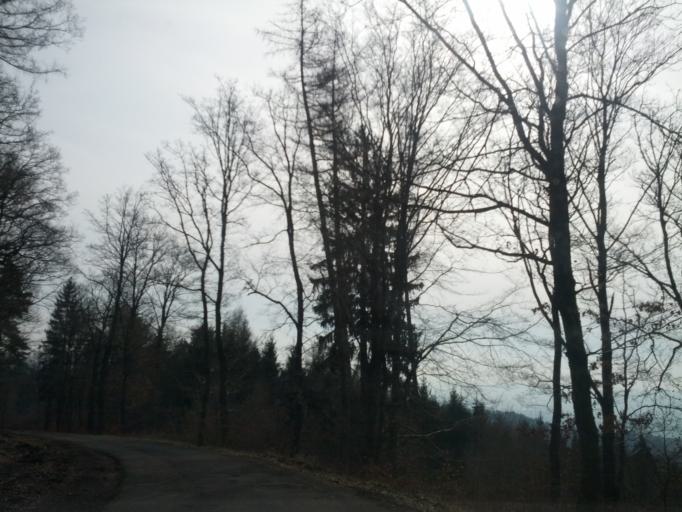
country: DE
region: Thuringia
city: Schweina
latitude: 50.8600
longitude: 10.3122
